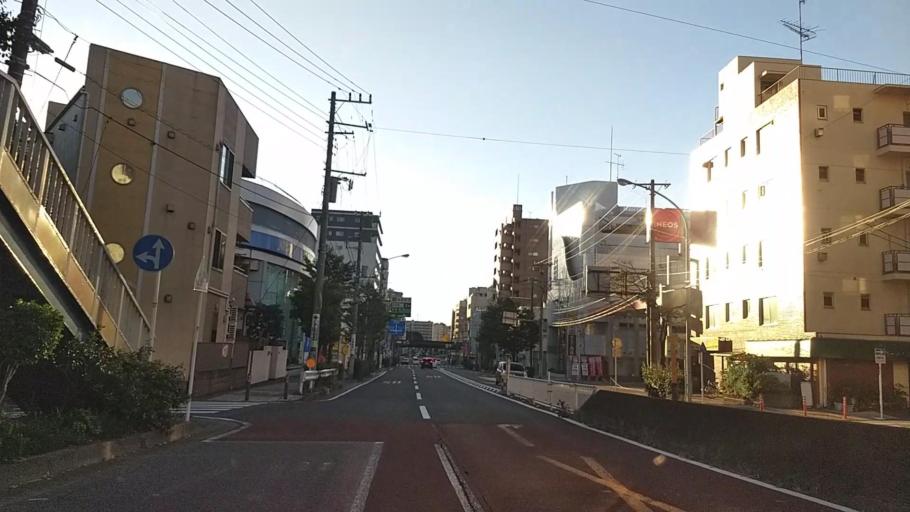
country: JP
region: Kanagawa
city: Yokohama
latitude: 35.4417
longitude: 139.6222
